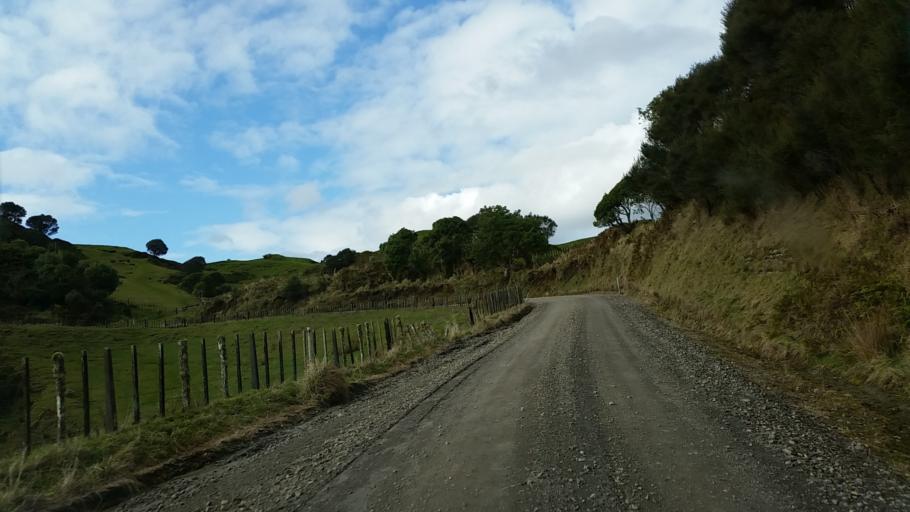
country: NZ
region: Taranaki
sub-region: South Taranaki District
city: Eltham
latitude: -39.1734
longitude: 174.6178
